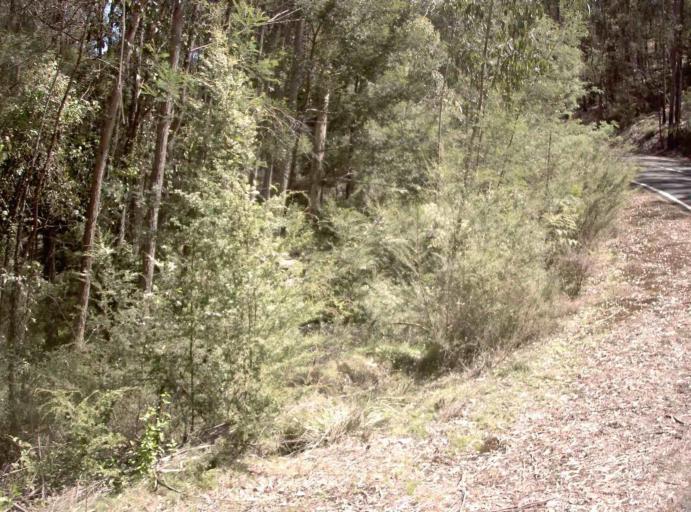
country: AU
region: Victoria
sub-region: East Gippsland
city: Lakes Entrance
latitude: -37.3855
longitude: 148.2187
